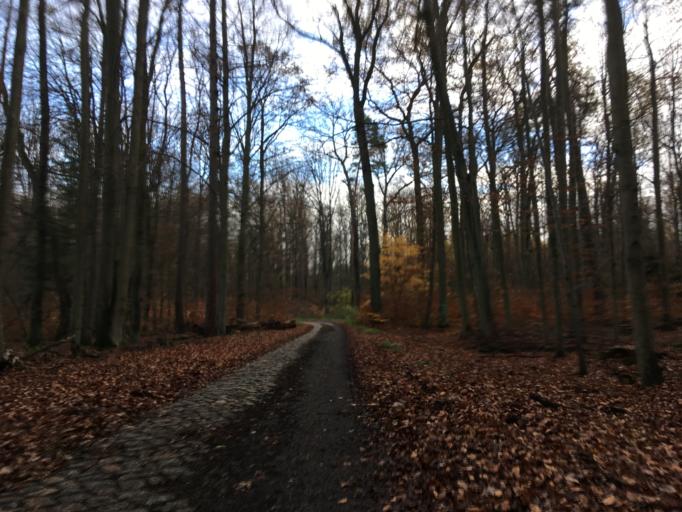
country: DE
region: Brandenburg
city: Tauer
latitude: 51.9395
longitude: 14.5100
